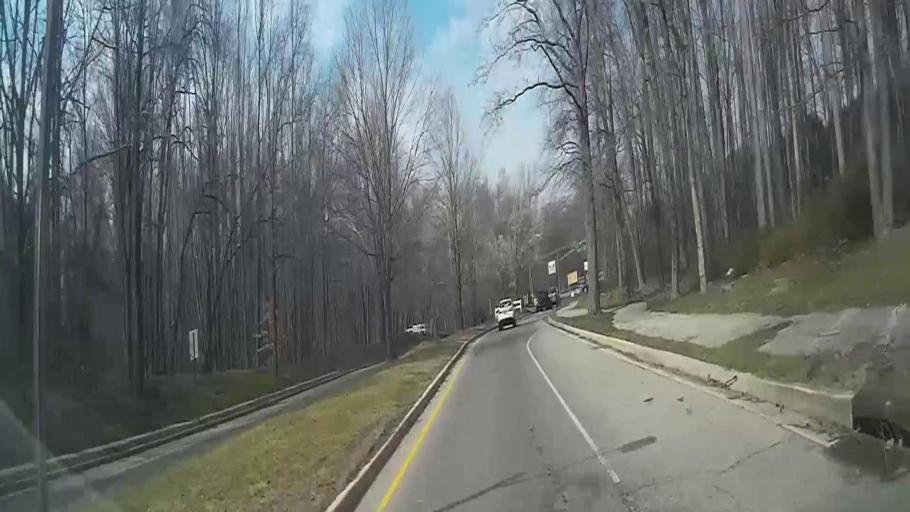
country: US
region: New Jersey
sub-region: Burlington County
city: Marlton
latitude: 39.8784
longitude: -74.8630
